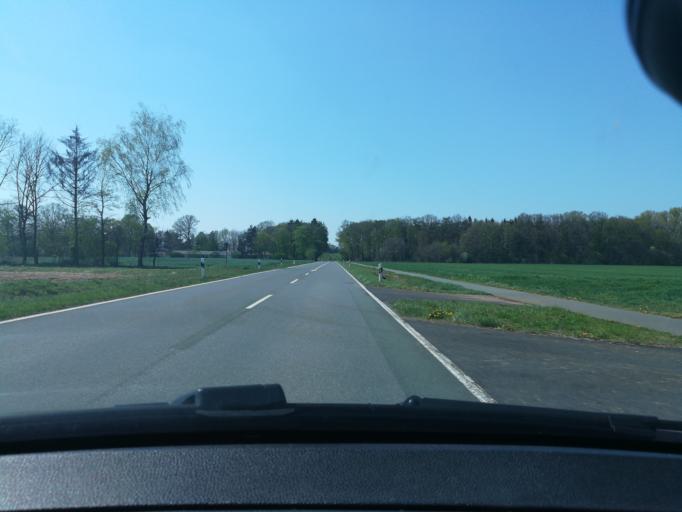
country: DE
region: North Rhine-Westphalia
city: Versmold
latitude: 52.0079
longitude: 8.1782
